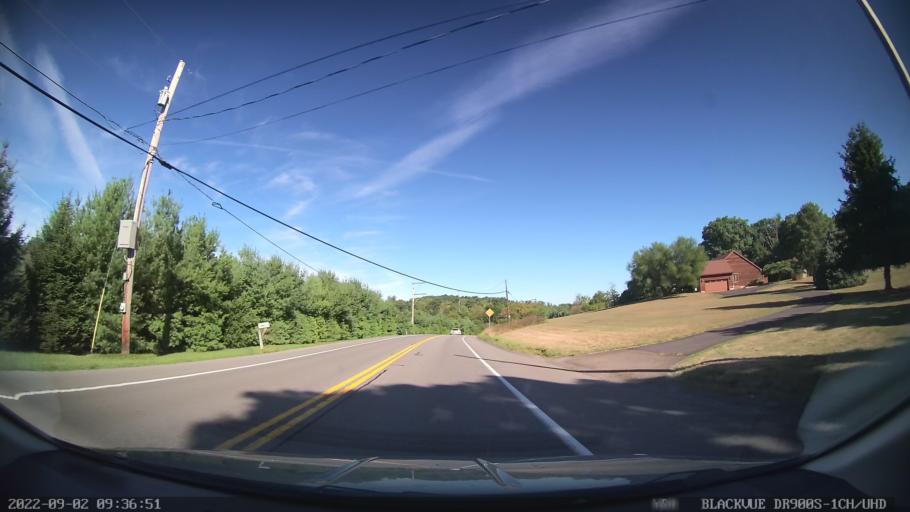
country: US
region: Pennsylvania
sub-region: Northumberland County
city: Elysburg
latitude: 40.8862
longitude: -76.5557
